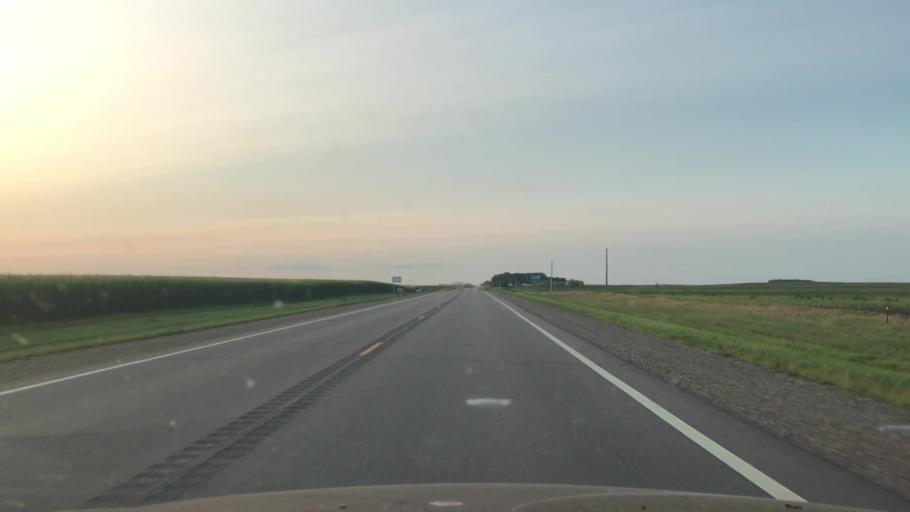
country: US
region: Minnesota
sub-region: Redwood County
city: Redwood Falls
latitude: 44.4349
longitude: -95.1176
